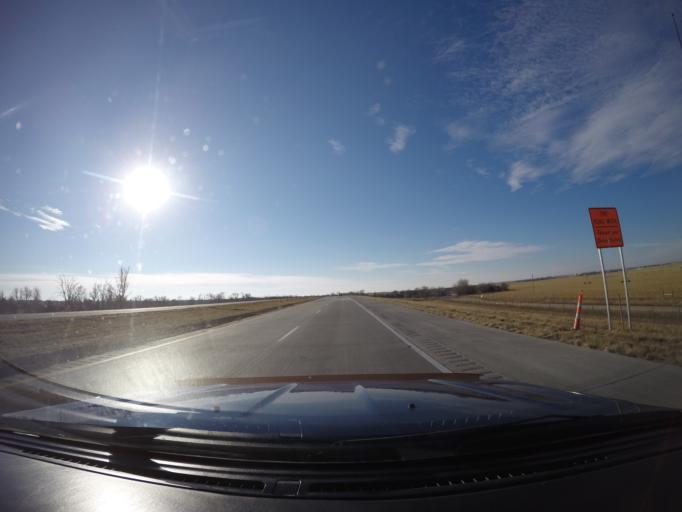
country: US
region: Nebraska
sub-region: Buffalo County
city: Kearney
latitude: 40.6797
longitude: -98.9907
